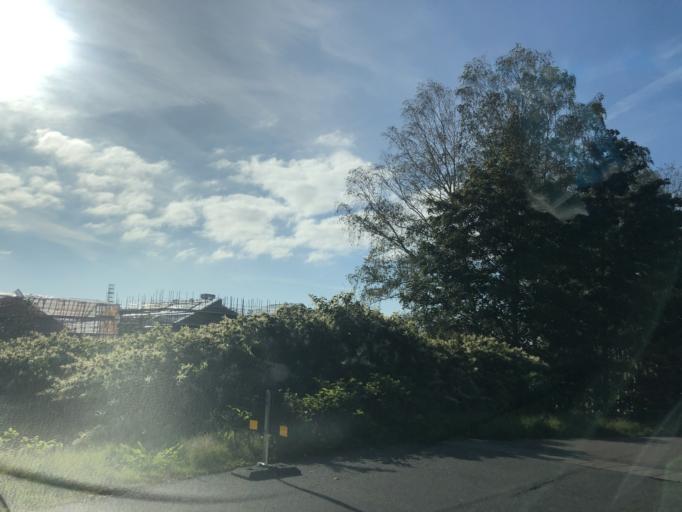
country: SE
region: Vaestra Goetaland
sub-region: Molndal
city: Moelndal
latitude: 57.6590
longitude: 12.0305
